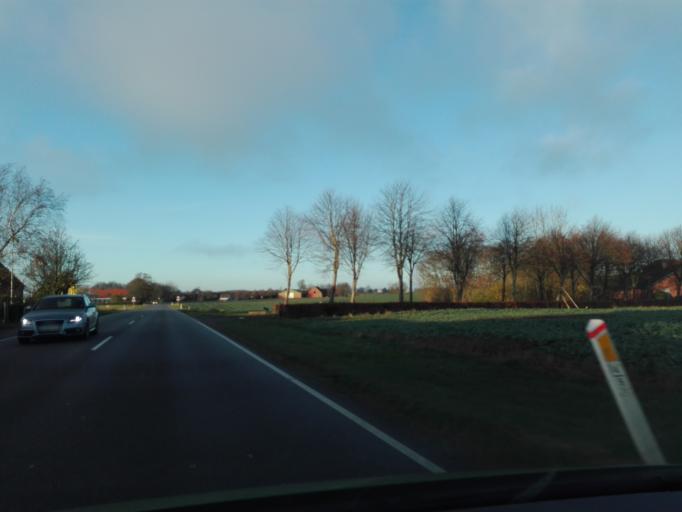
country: DK
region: Central Jutland
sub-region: Skanderborg Kommune
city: Skanderborg
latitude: 56.0662
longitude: 9.8980
